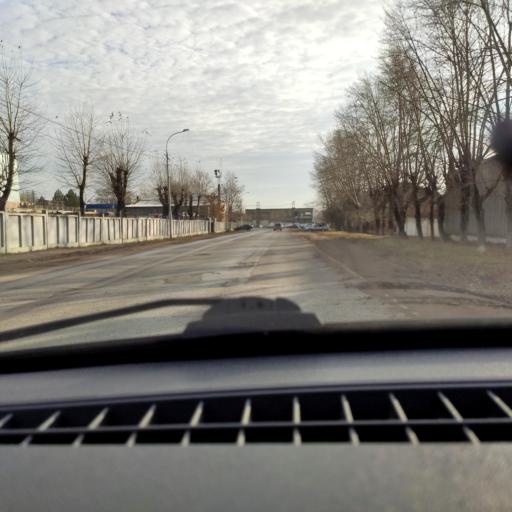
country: RU
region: Bashkortostan
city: Ufa
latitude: 54.8407
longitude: 56.0793
